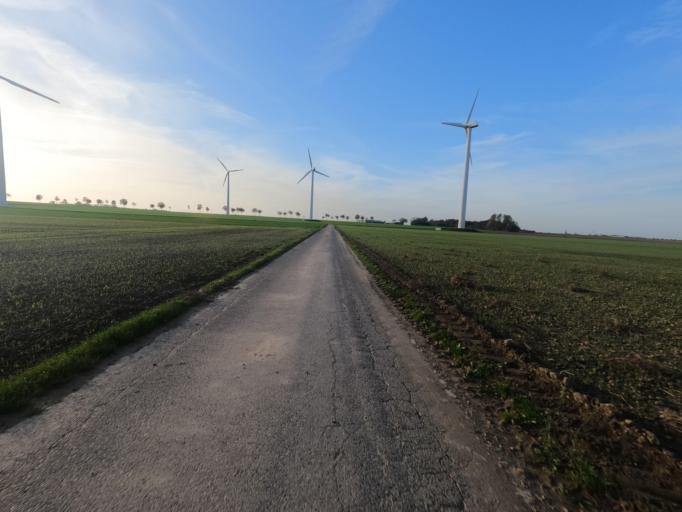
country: DE
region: North Rhine-Westphalia
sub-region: Regierungsbezirk Koln
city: Titz
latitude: 51.0482
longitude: 6.3781
